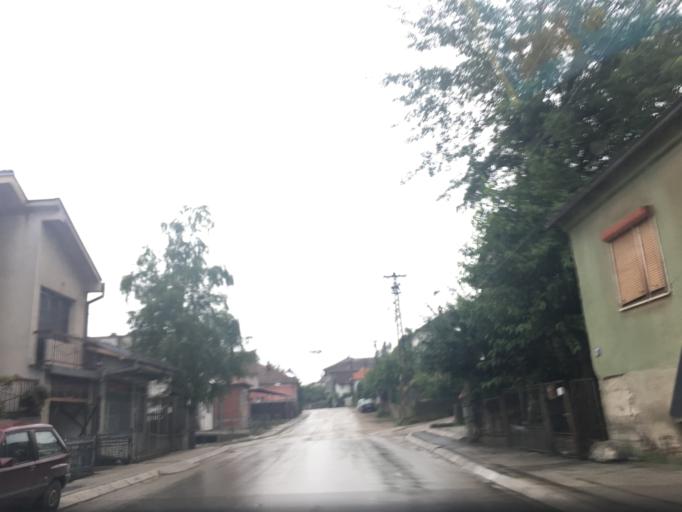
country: RS
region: Central Serbia
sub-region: Nisavski Okrug
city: Aleksinac
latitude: 43.5459
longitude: 21.7061
